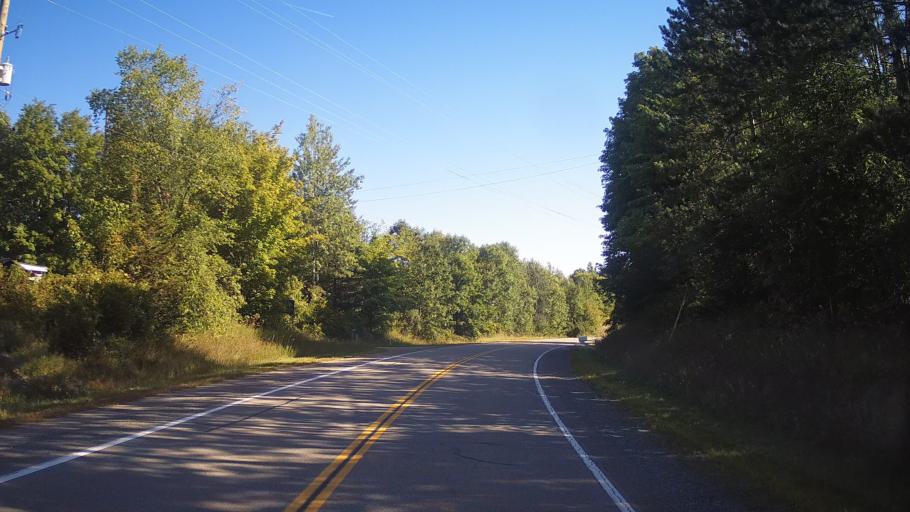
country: CA
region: Ontario
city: Gananoque
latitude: 44.5835
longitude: -76.1109
